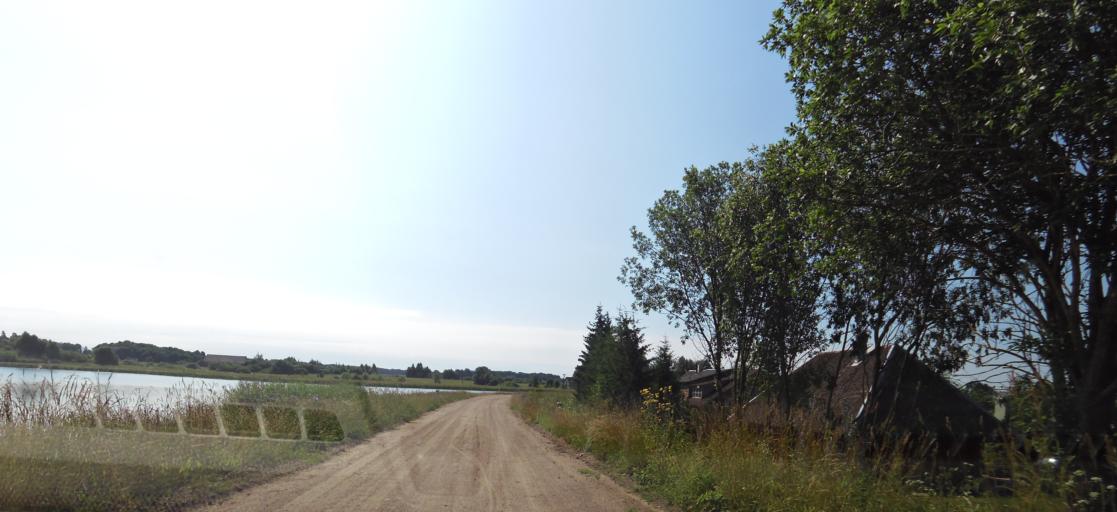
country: LT
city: Grigiskes
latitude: 54.8654
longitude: 25.0612
